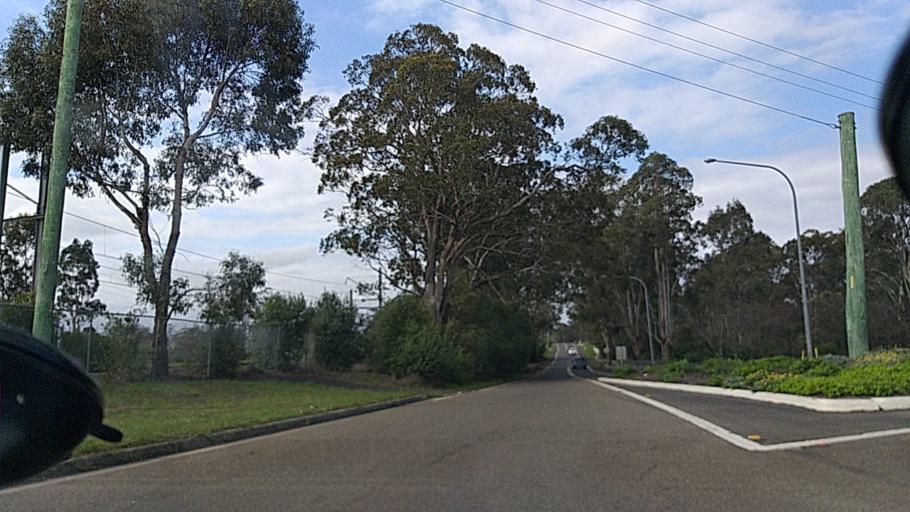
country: AU
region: New South Wales
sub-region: Campbelltown Municipality
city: Glen Alpine
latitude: -34.0780
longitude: 150.7840
